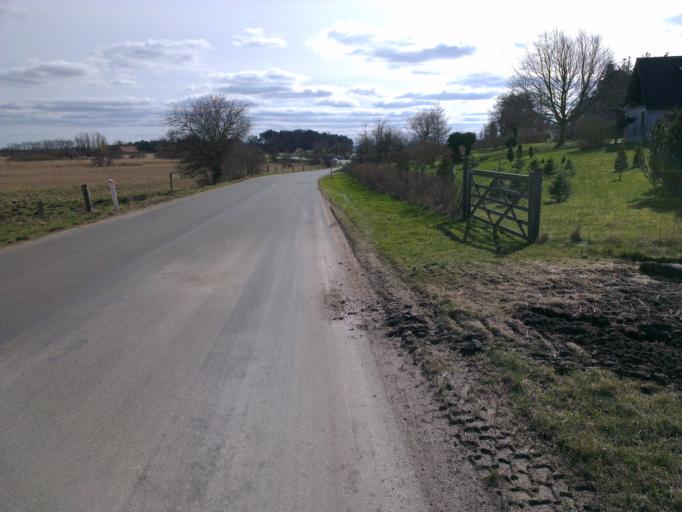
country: DK
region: Capital Region
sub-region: Frederikssund Kommune
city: Skibby
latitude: 55.7436
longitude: 11.9874
